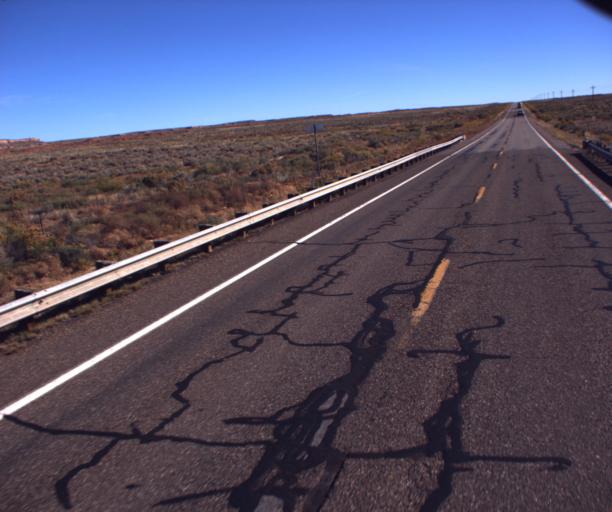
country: US
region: Arizona
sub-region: Coconino County
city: Fredonia
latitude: 36.8667
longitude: -112.6968
